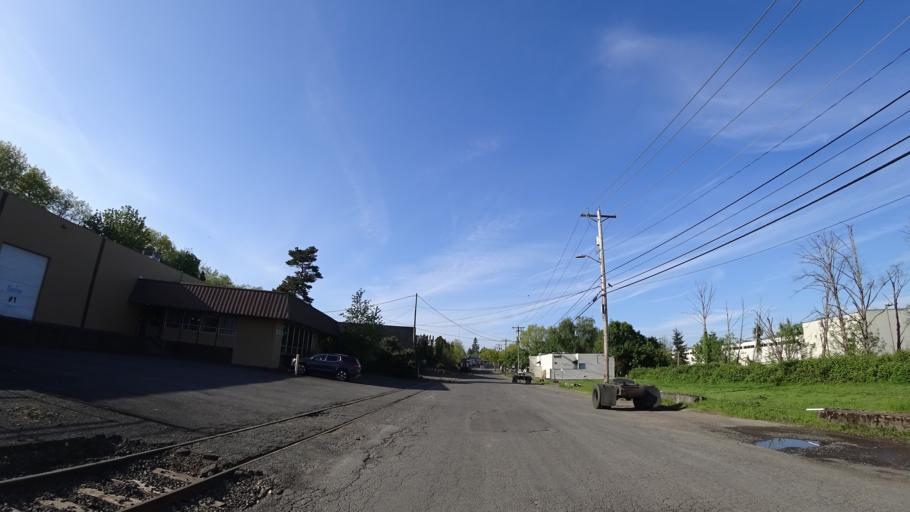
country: US
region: Oregon
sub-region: Clackamas County
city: Milwaukie
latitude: 45.4553
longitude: -122.6437
